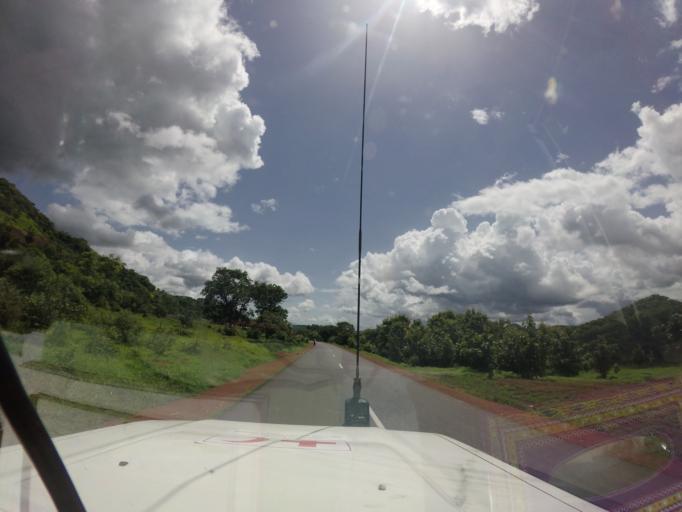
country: SL
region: Northern Province
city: Bindi
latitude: 10.1468
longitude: -11.5953
